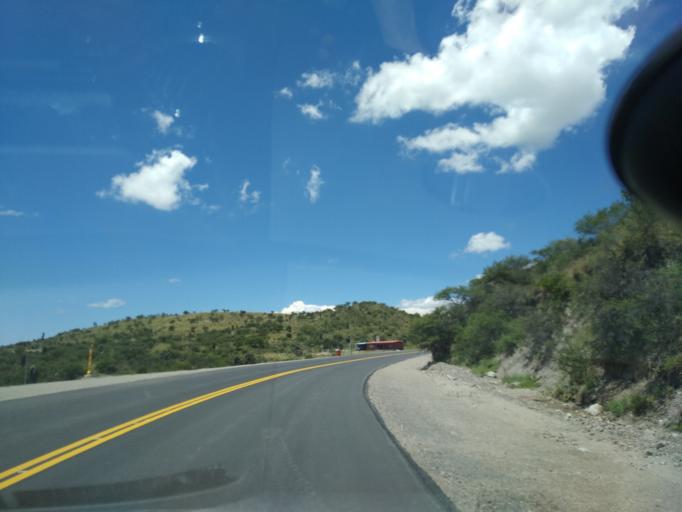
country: AR
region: Cordoba
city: Salsacate
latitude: -31.3755
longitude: -65.2890
